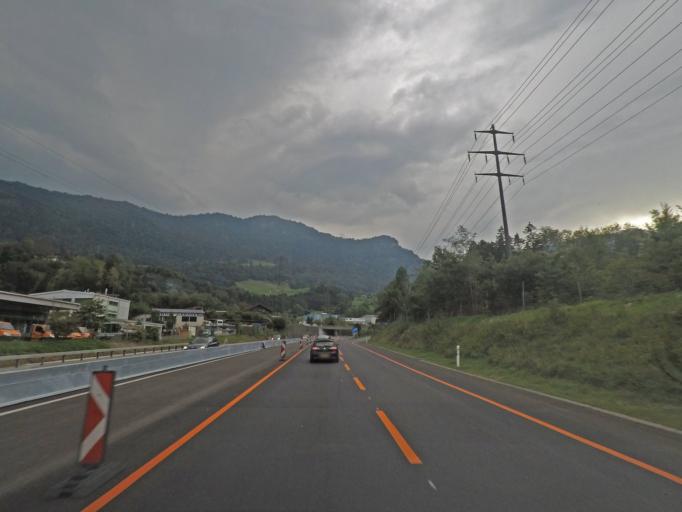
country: CH
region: Schwyz
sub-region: Bezirk Schwyz
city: Goldau
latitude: 47.0437
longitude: 8.5531
